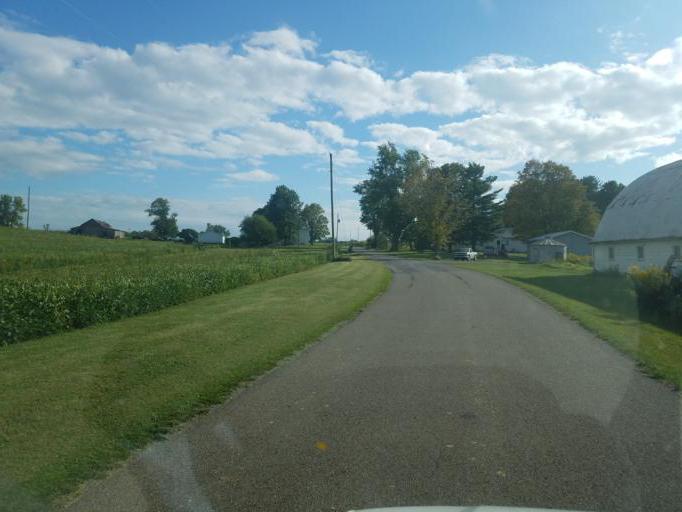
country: US
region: Ohio
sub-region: Knox County
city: Fredericktown
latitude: 40.4350
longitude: -82.5696
